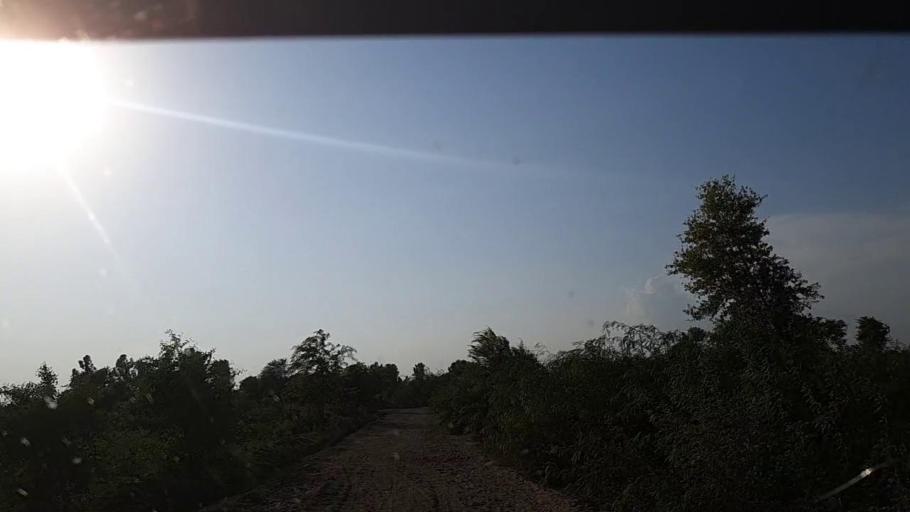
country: PK
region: Sindh
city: Pano Aqil
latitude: 27.9081
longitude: 69.2027
